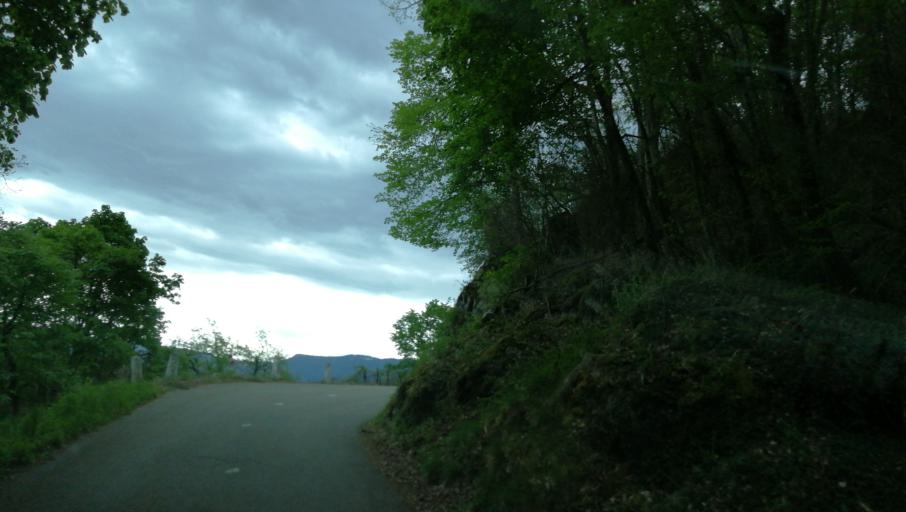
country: FR
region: Rhone-Alpes
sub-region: Departement de la Savoie
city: Chatillon
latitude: 45.7581
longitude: 5.8284
